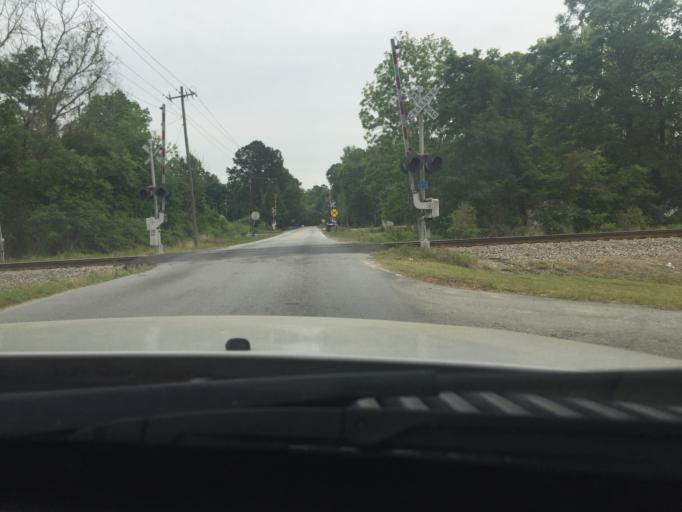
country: US
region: Georgia
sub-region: Chatham County
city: Georgetown
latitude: 31.9752
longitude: -81.2476
